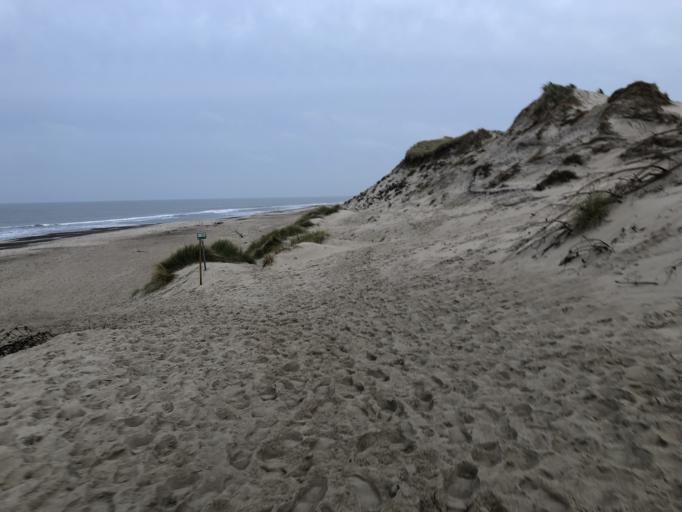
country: DK
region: Central Jutland
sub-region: Holstebro Kommune
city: Ulfborg
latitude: 56.2904
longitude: 8.1263
